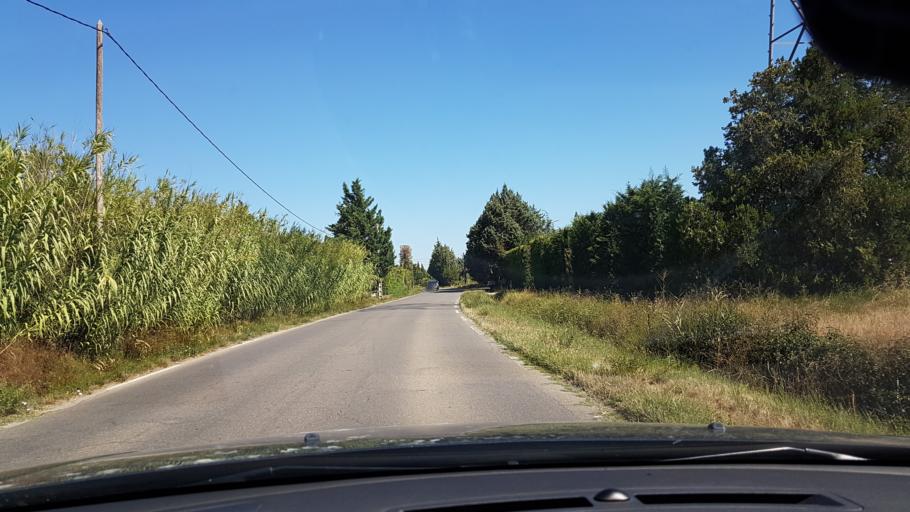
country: FR
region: Provence-Alpes-Cote d'Azur
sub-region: Departement des Bouches-du-Rhone
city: Molleges
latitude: 43.7905
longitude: 4.9537
